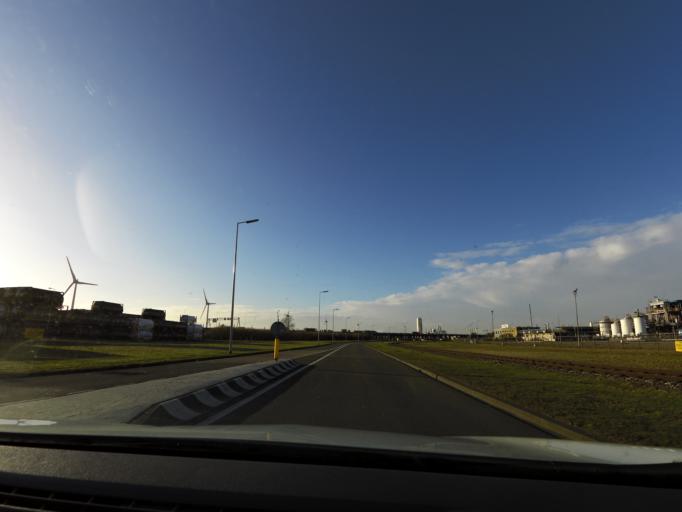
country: NL
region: South Holland
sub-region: Gemeente Maassluis
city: Maassluis
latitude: 51.8704
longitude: 4.2721
